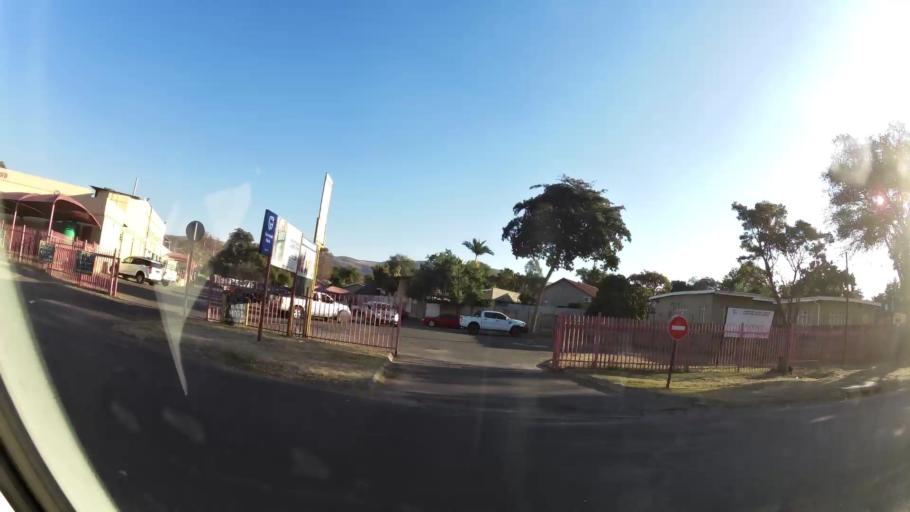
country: ZA
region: North-West
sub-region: Bojanala Platinum District Municipality
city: Rustenburg
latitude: -25.6798
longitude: 27.2157
